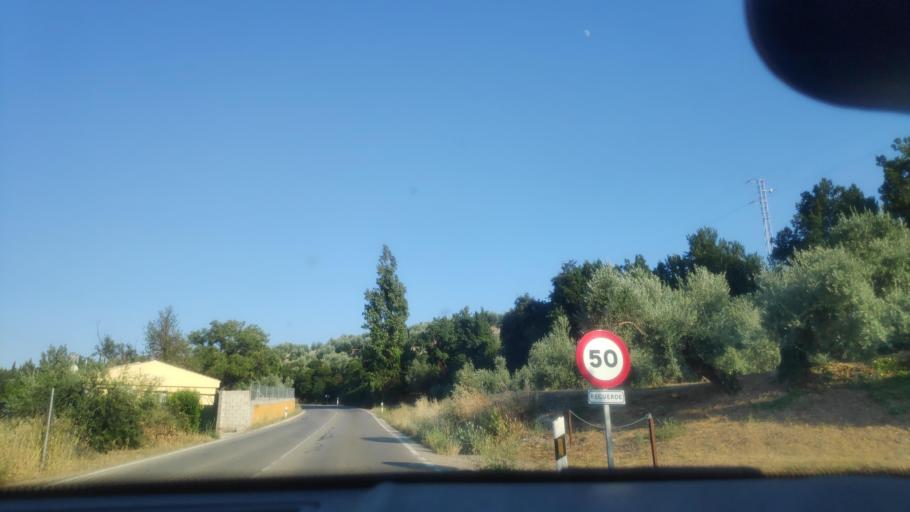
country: ES
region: Andalusia
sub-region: Provincia de Jaen
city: Jaen
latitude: 37.7488
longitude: -3.7936
